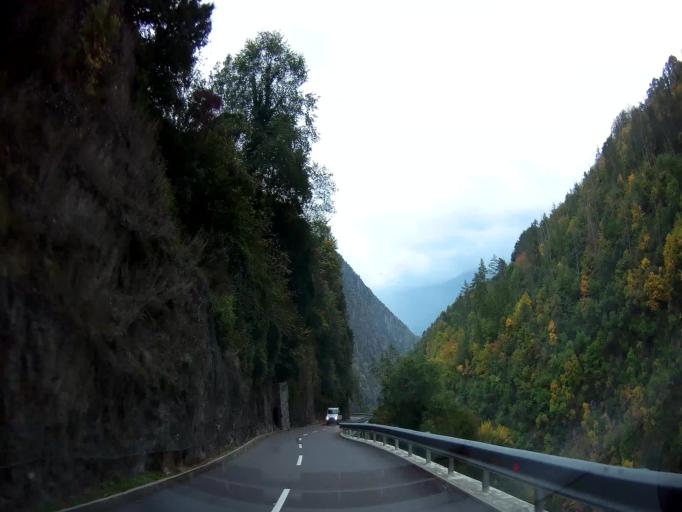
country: IT
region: Trentino-Alto Adige
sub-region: Bolzano
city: Naturno
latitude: 46.6569
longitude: 10.9608
